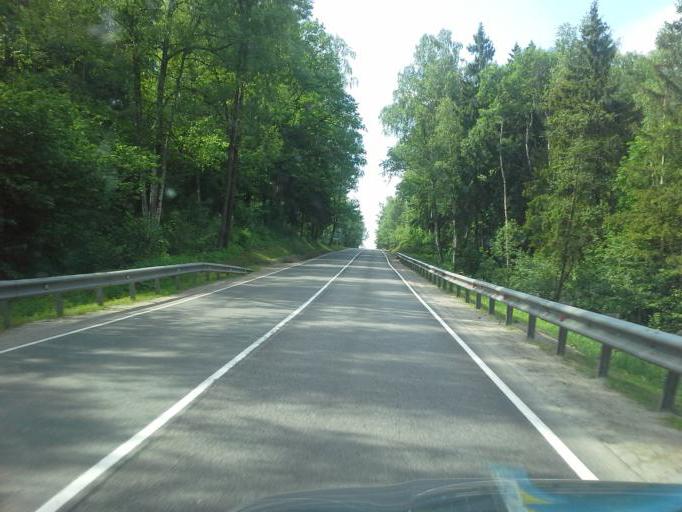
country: RU
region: Moskovskaya
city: Gorki Vtoryye
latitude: 55.7103
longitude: 37.2084
